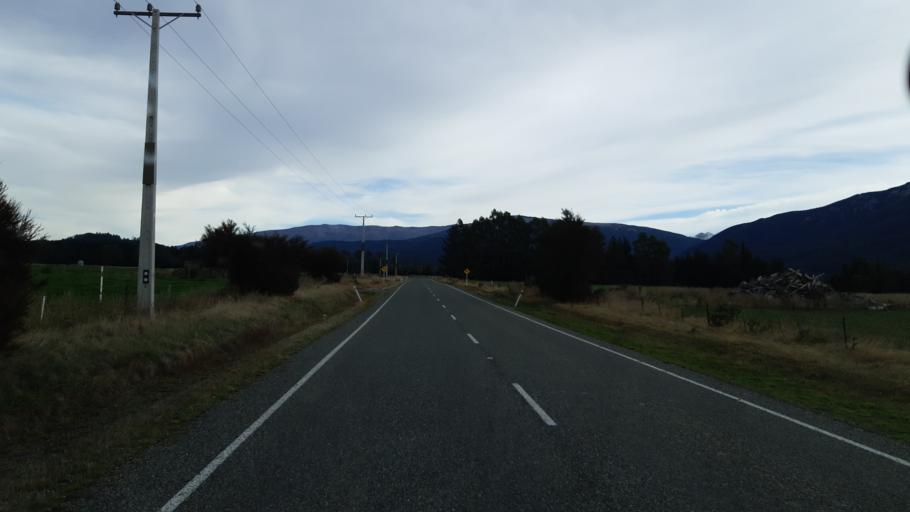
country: NZ
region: Tasman
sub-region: Tasman District
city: Brightwater
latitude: -41.6533
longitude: 173.2617
